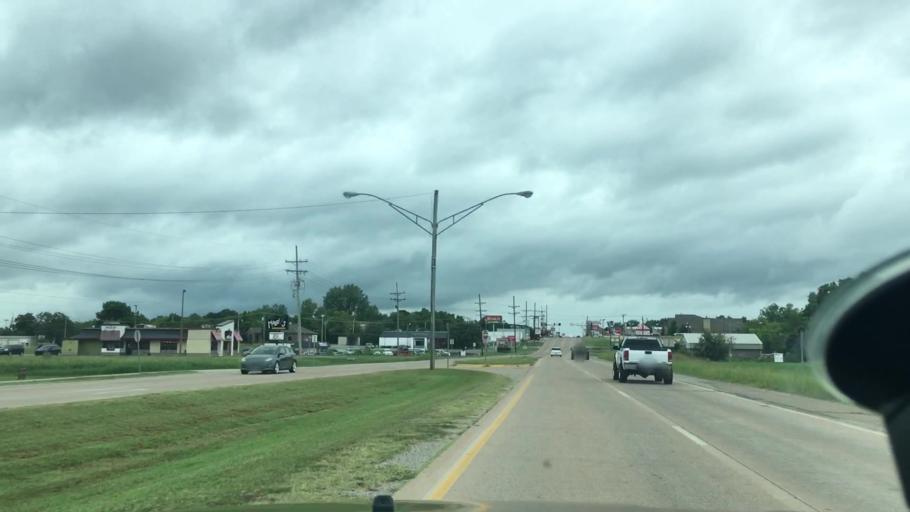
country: US
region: Oklahoma
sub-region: Seminole County
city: Seminole
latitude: 35.2363
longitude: -96.6712
